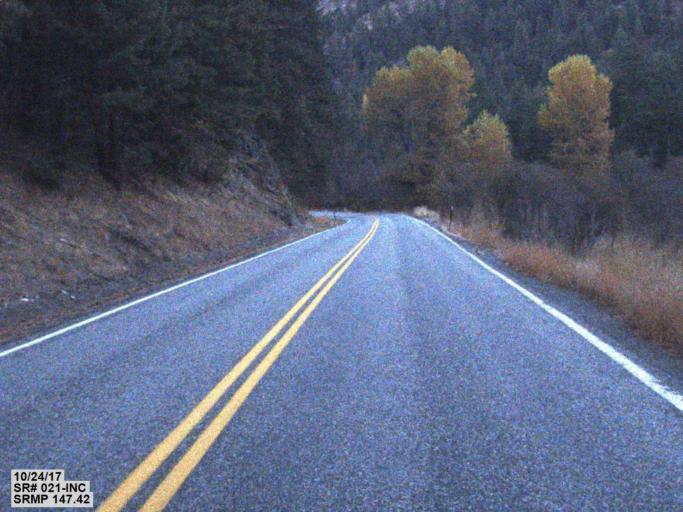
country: US
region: Washington
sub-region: Ferry County
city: Republic
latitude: 48.4752
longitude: -118.7325
